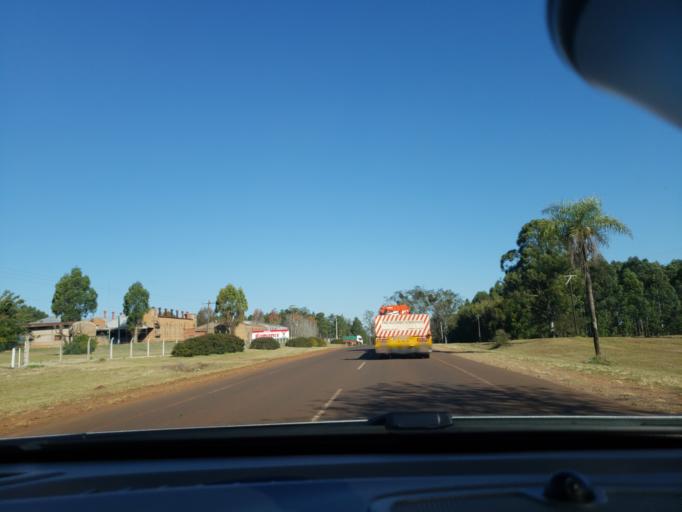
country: AR
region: Misiones
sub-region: Departamento de Apostoles
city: San Jose
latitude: -27.8101
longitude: -55.7683
